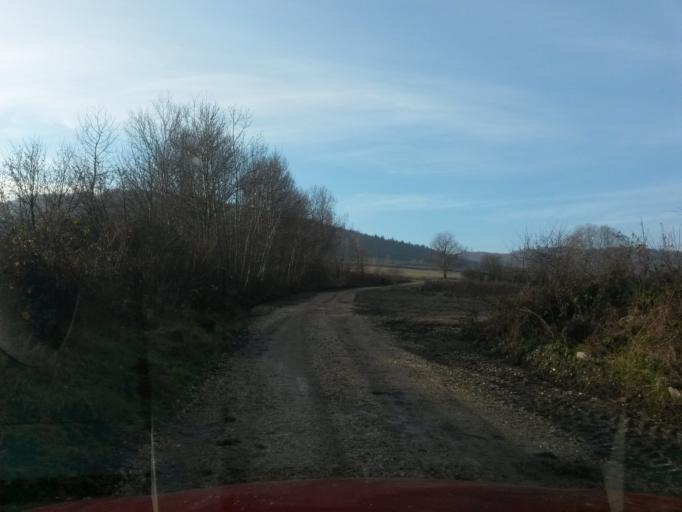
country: SK
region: Kosicky
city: Roznava
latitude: 48.7100
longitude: 20.4470
